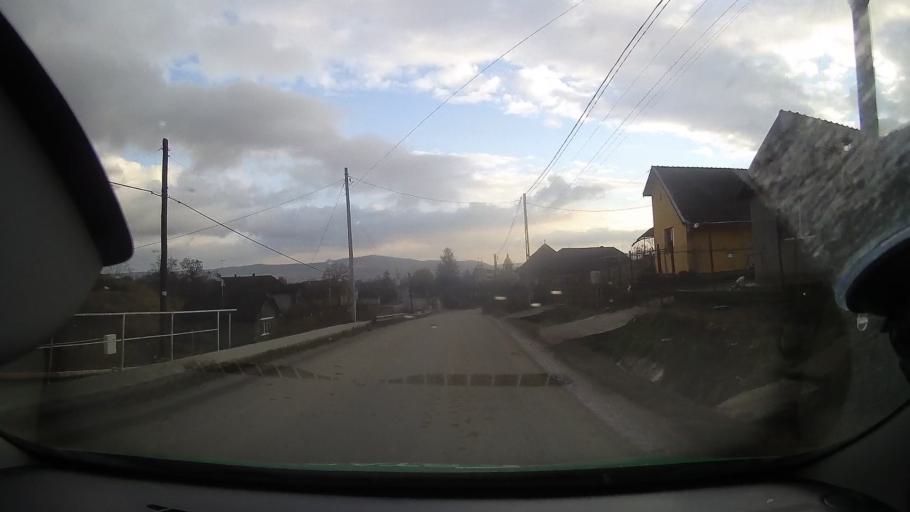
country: RO
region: Alba
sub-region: Comuna Lunca Muresului
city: Lunca Muresului
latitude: 46.4309
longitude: 23.9089
